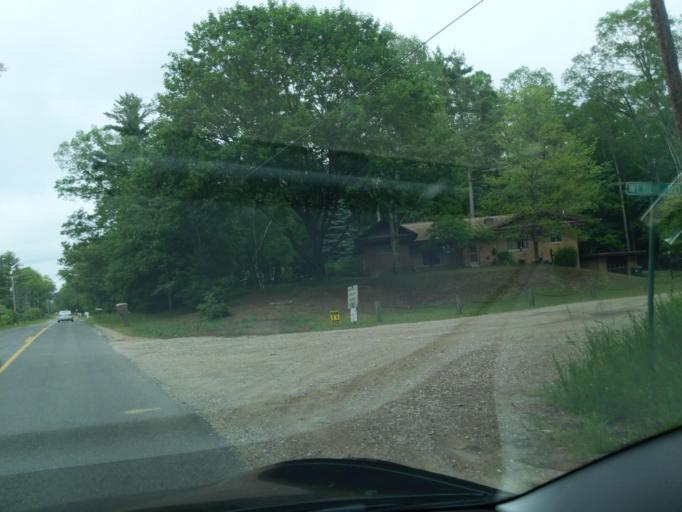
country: US
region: Michigan
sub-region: Muskegon County
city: North Muskegon
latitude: 43.2538
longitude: -86.3222
